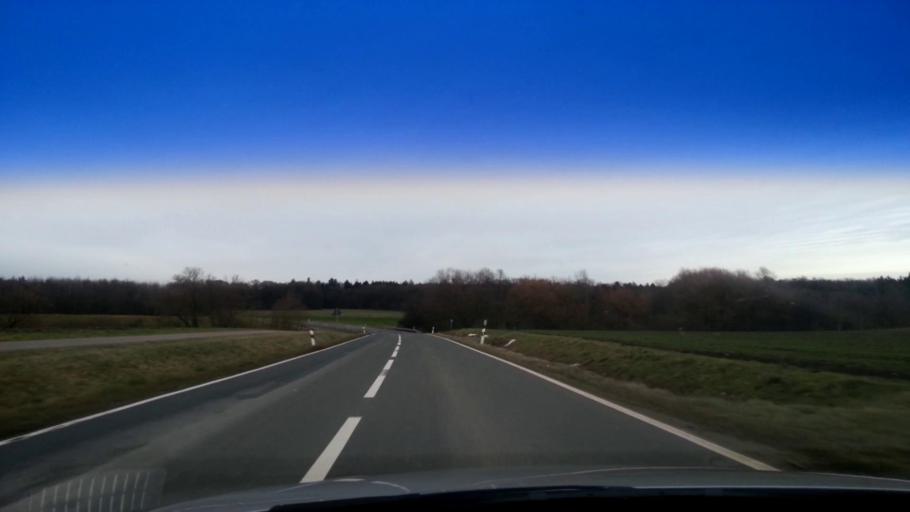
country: DE
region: Bavaria
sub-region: Upper Franconia
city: Litzendorf
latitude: 49.8872
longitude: 11.0104
